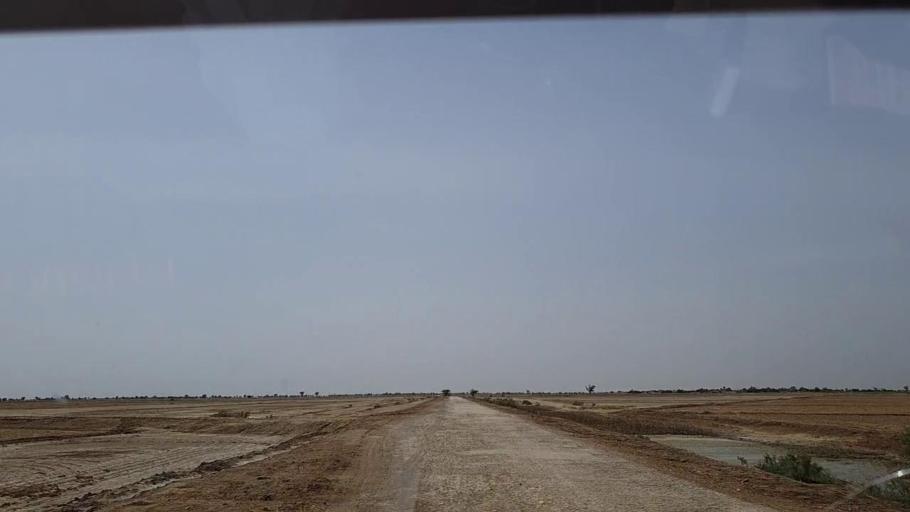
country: PK
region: Sindh
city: Johi
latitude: 26.7383
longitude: 67.6329
